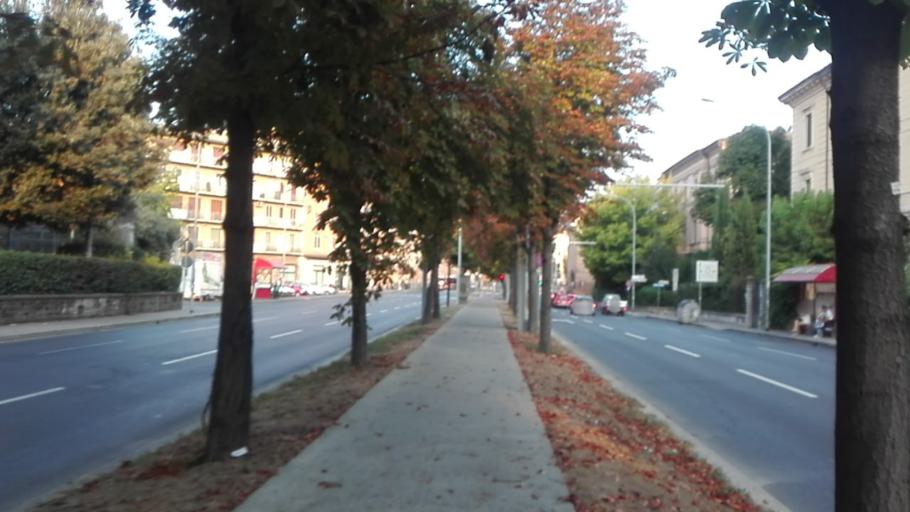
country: IT
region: Emilia-Romagna
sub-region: Provincia di Bologna
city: Bologna
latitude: 44.4852
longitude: 11.3498
